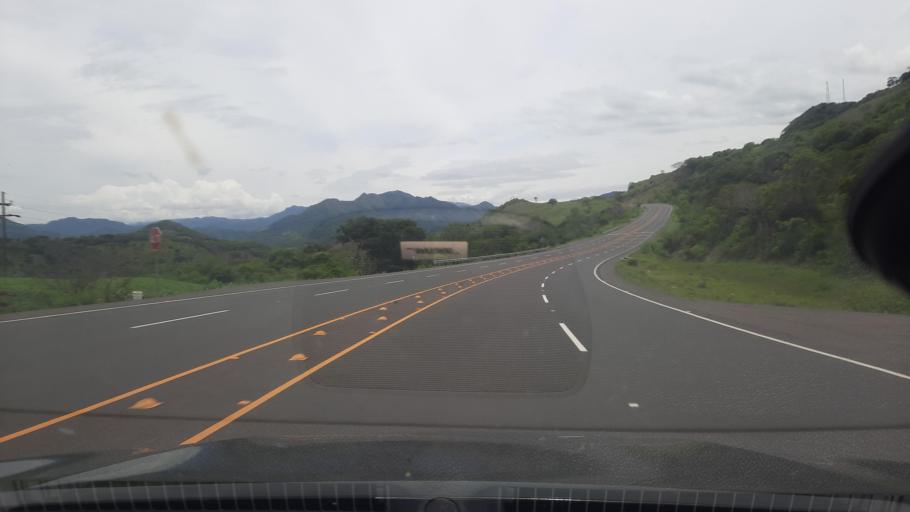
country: HN
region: Valle
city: Aramecina
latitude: 13.7940
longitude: -87.7048
